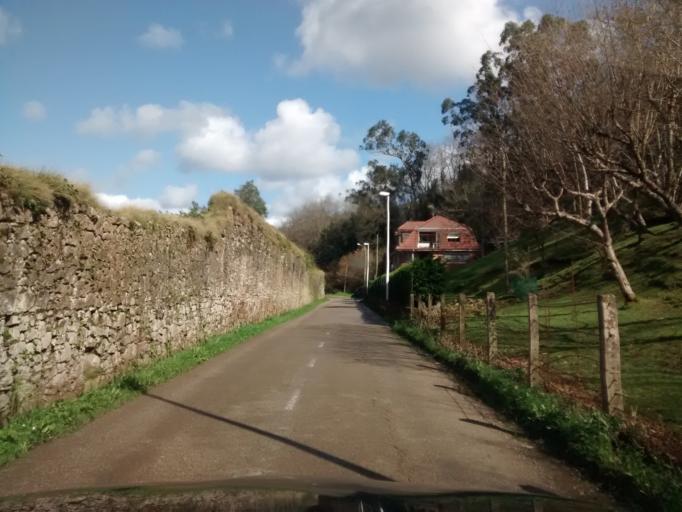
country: ES
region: Cantabria
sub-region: Provincia de Cantabria
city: Lierganes
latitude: 43.3488
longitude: -3.7089
